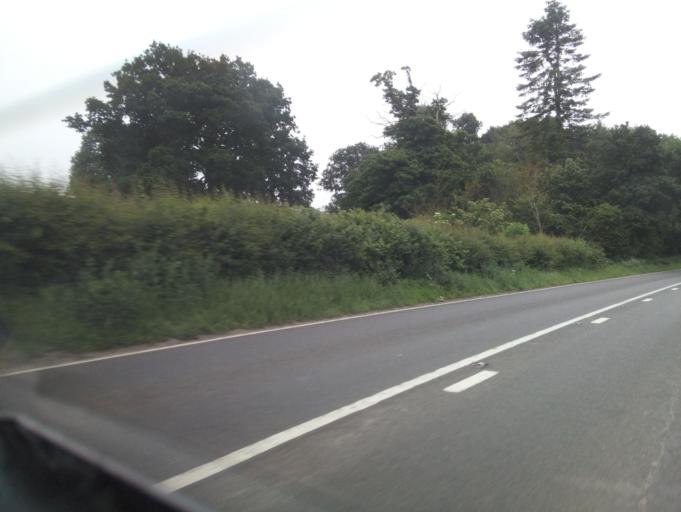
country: GB
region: England
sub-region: Derbyshire
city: Netherseal
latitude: 52.7050
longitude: -1.5549
